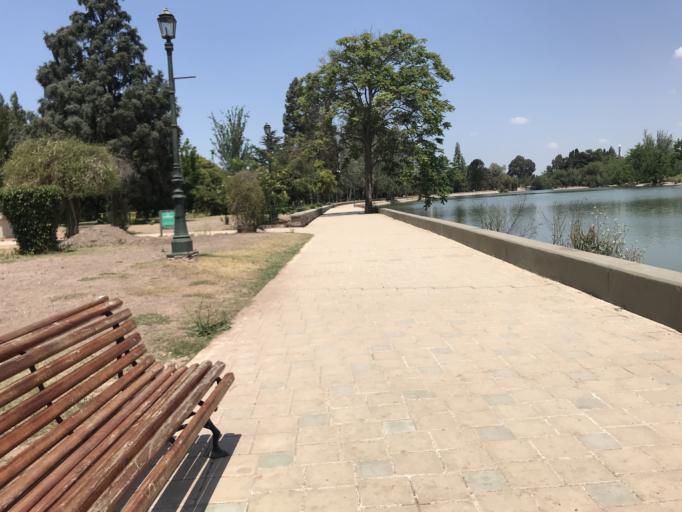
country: AR
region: Mendoza
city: Mendoza
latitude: -32.8933
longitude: -68.8658
